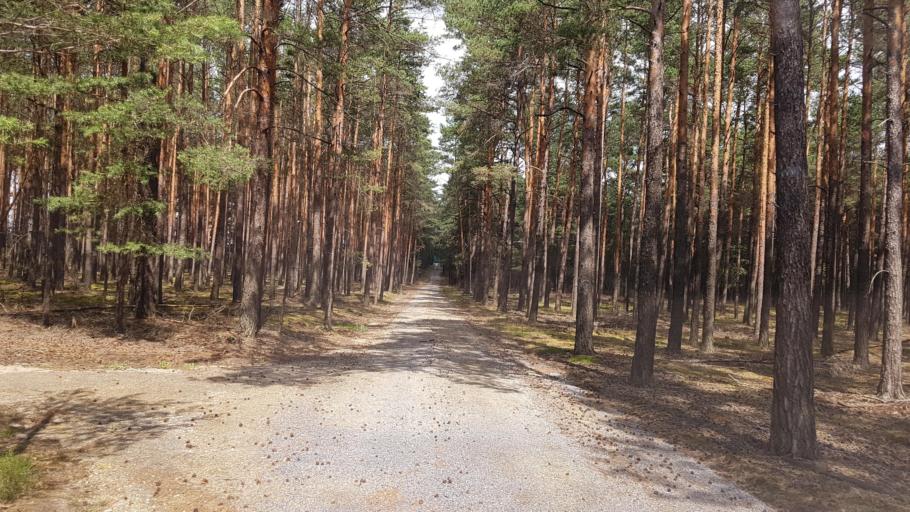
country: DE
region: Brandenburg
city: Crinitz
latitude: 51.7062
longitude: 13.8199
